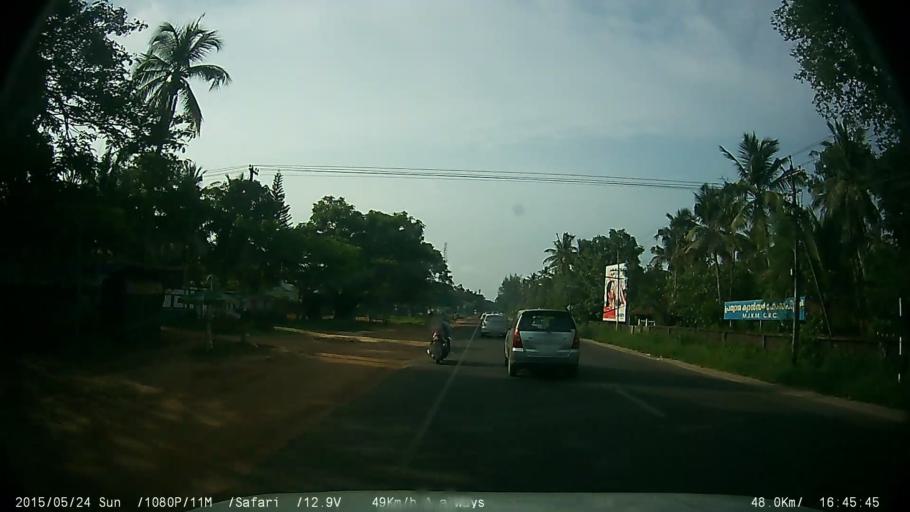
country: IN
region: Kerala
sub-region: Alappuzha
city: Shertallai
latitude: 9.6640
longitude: 76.3387
